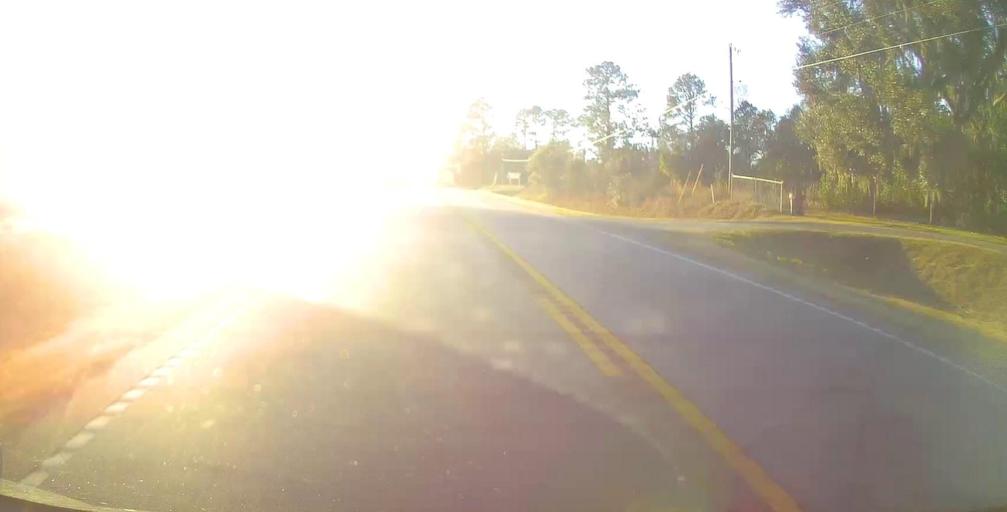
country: US
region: Georgia
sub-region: Dougherty County
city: Albany
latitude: 31.5041
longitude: -84.2208
